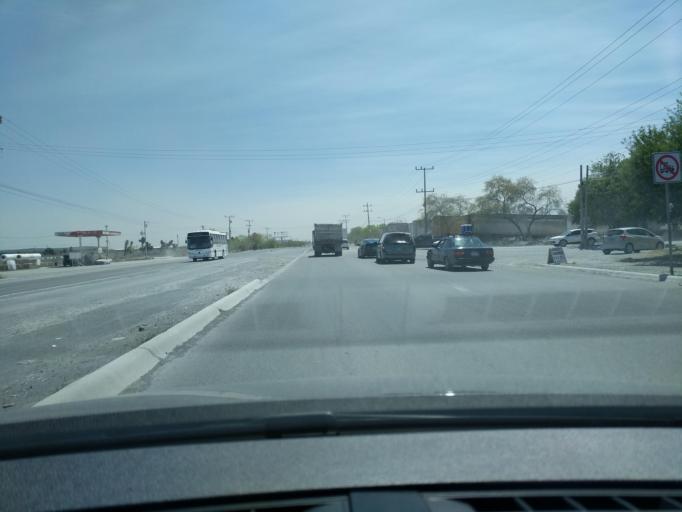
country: MX
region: Nuevo Leon
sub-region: Salinas Victoria
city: Emiliano Zapata
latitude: 25.8900
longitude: -100.2584
